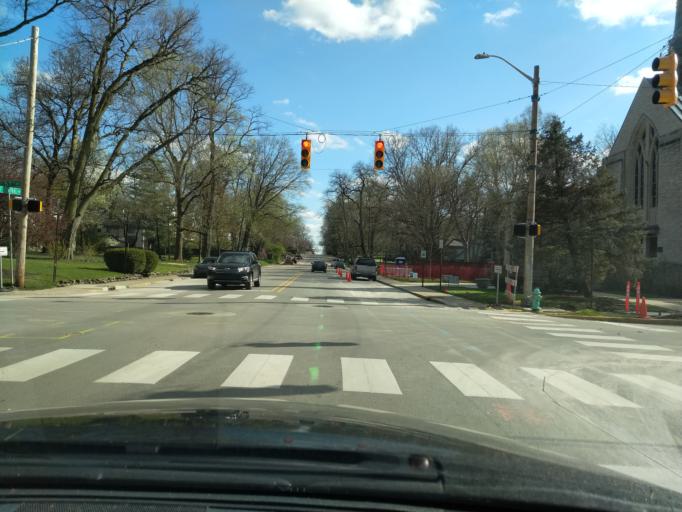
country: US
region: Indiana
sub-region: Marion County
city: Broad Ripple
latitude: 39.8573
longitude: -86.1502
